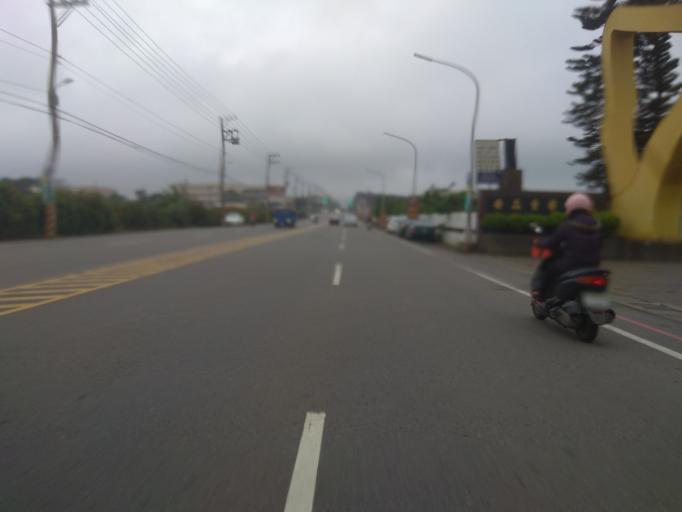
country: TW
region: Taiwan
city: Taoyuan City
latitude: 25.0278
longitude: 121.1090
